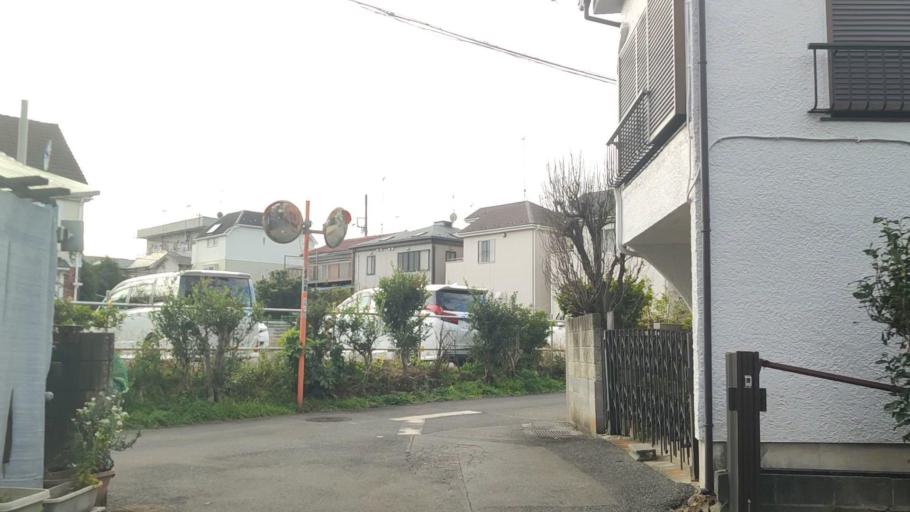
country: JP
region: Kanagawa
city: Minami-rinkan
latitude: 35.4927
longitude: 139.4338
